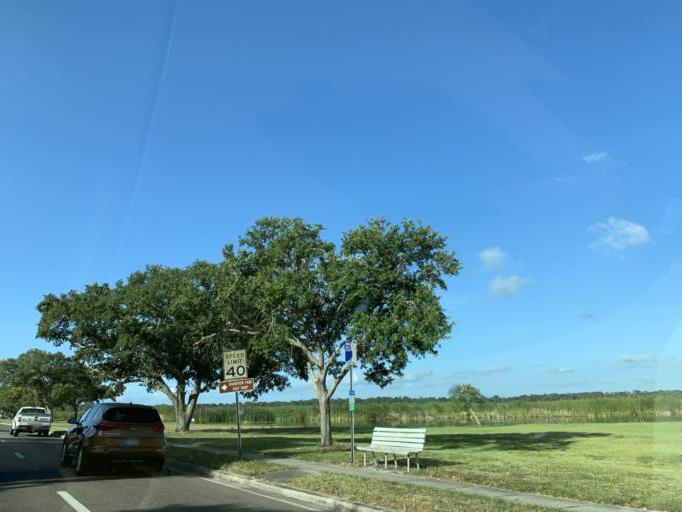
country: US
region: Florida
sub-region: Pinellas County
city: Saint Petersburg
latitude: 27.7412
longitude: -82.6466
